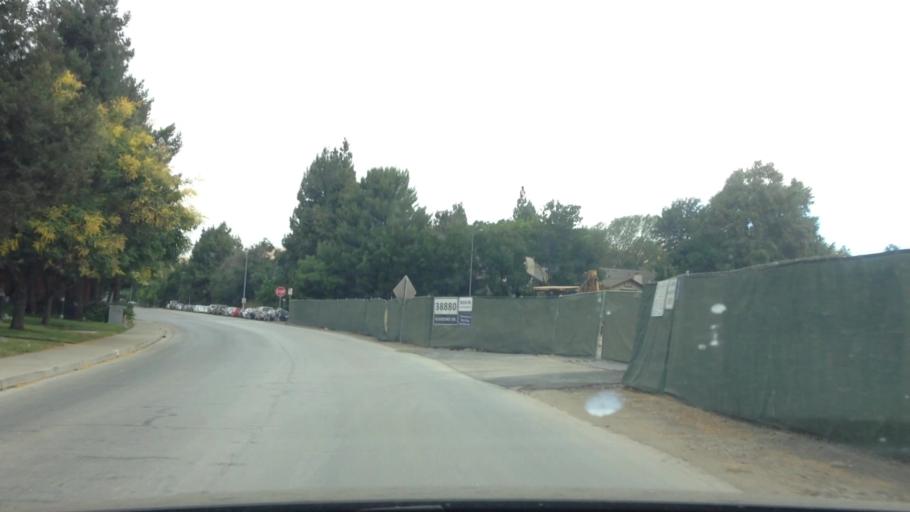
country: US
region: California
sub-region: Alameda County
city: Fremont
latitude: 37.5609
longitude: -121.9722
